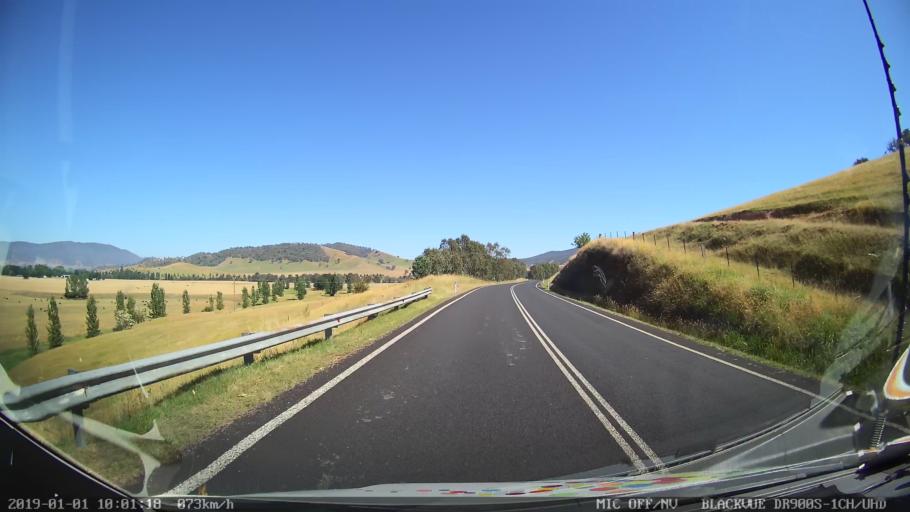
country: AU
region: New South Wales
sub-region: Snowy River
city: Jindabyne
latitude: -36.1929
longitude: 148.1021
